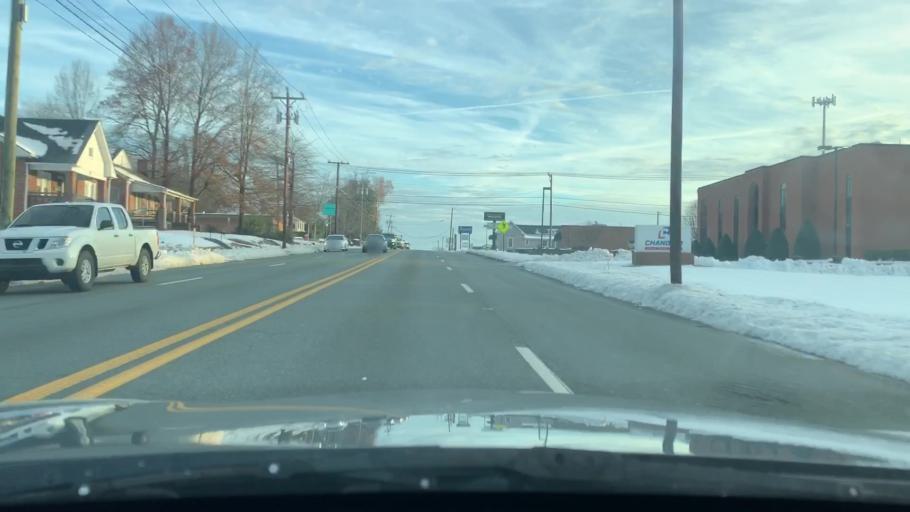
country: US
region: North Carolina
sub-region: Alamance County
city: Burlington
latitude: 36.0903
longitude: -79.4463
